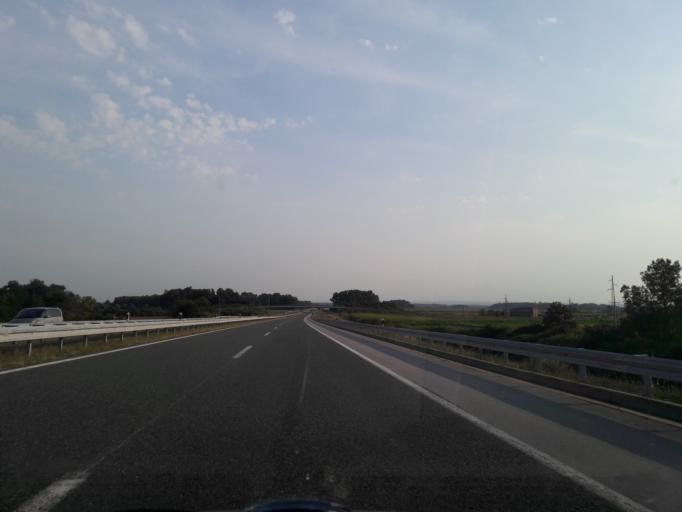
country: HR
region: Brodsko-Posavska
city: Vrpolje
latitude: 45.1998
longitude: 18.3327
